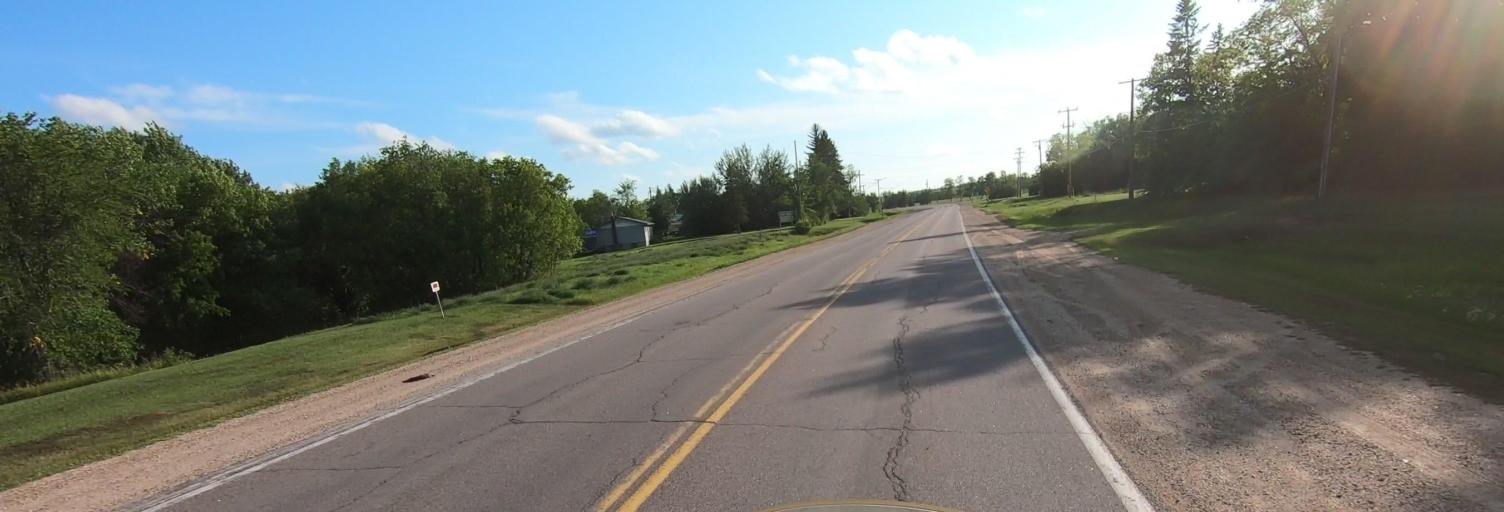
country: CA
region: Manitoba
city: Selkirk
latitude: 50.1683
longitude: -96.8641
